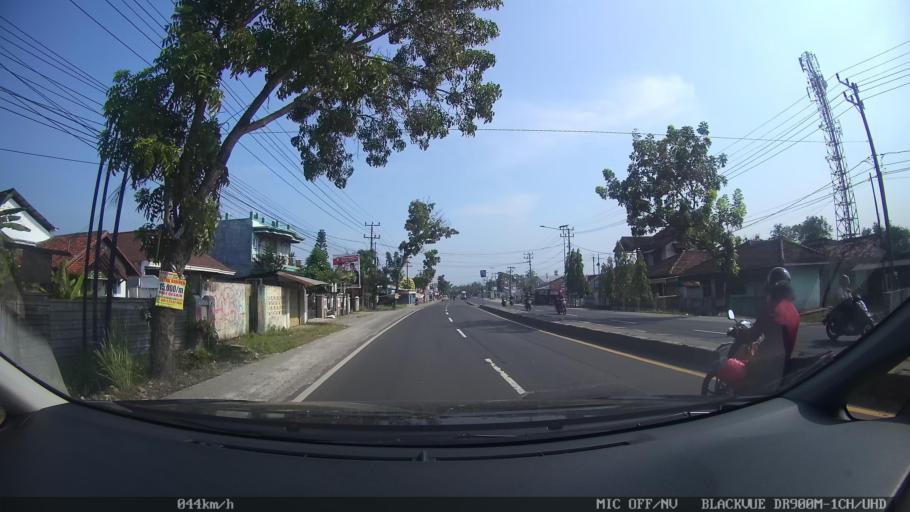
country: ID
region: Lampung
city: Natar
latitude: -5.2683
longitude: 105.1860
